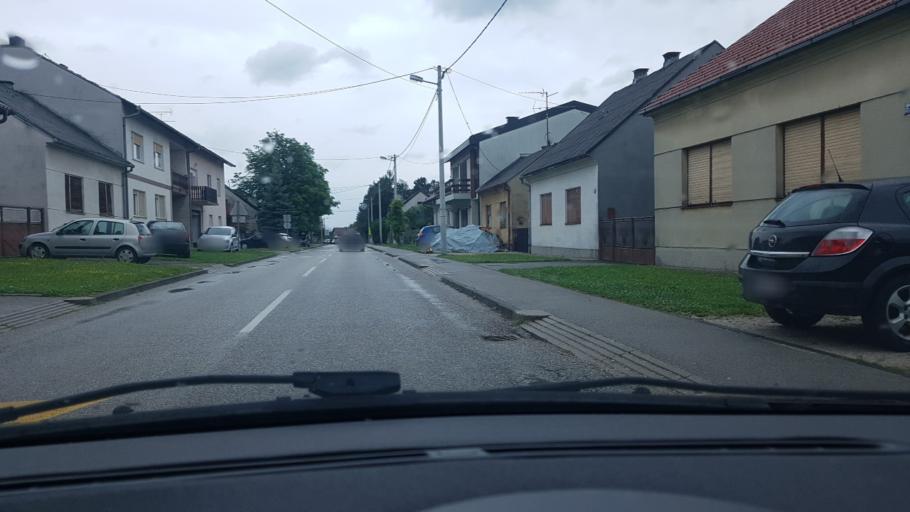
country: HR
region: Zagrebacka
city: Jastrebarsko
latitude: 45.6663
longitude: 15.6488
